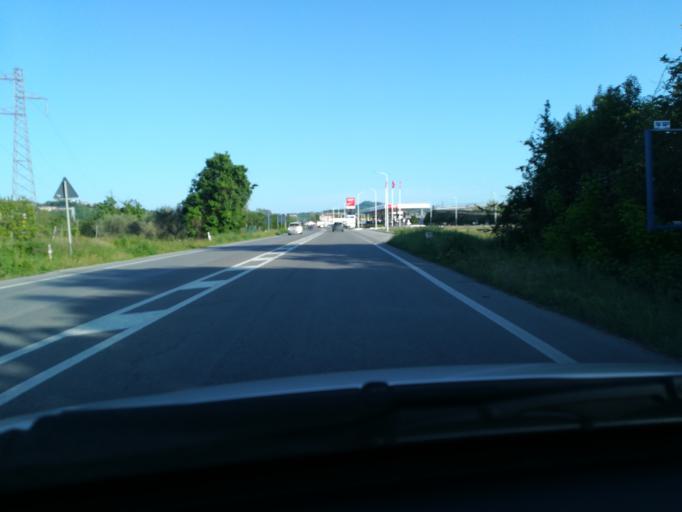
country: IT
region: Emilia-Romagna
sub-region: Provincia di Rimini
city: Cattolica
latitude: 43.9538
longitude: 12.7304
